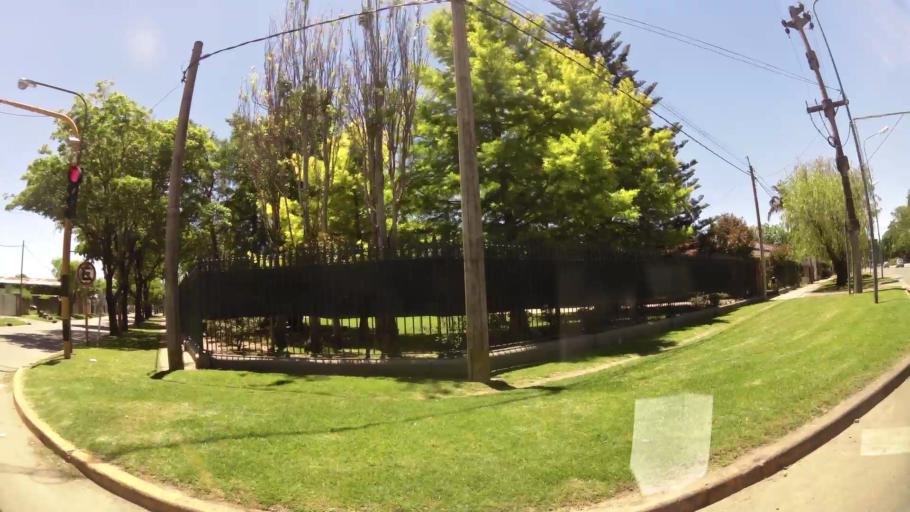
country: AR
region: Santa Fe
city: Rafaela
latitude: -31.2573
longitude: -61.4646
